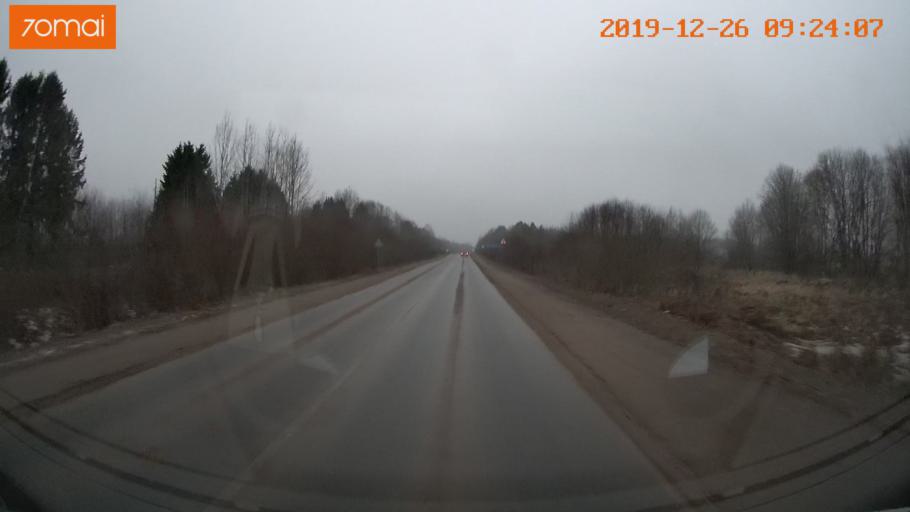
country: RU
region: Vologda
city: Gryazovets
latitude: 58.9970
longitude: 40.2021
